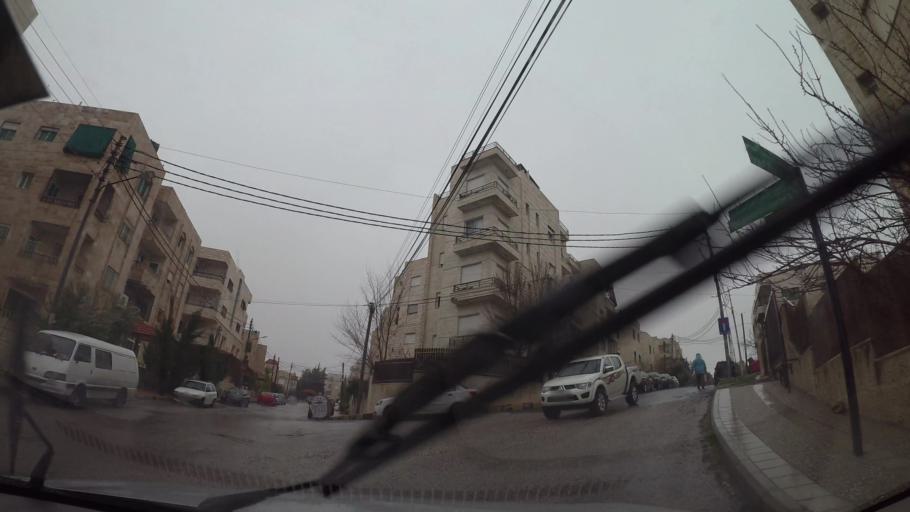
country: JO
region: Amman
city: Al Jubayhah
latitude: 32.0286
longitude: 35.8491
